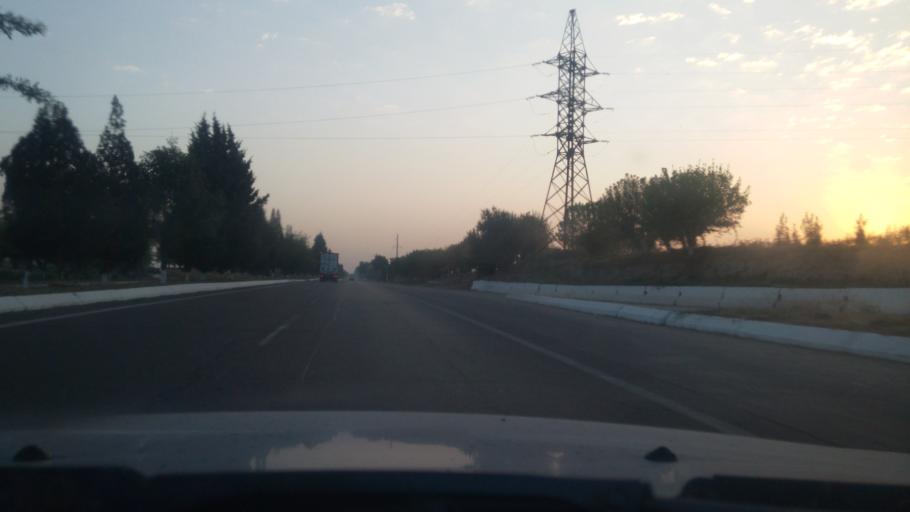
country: UZ
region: Toshkent
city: Zafar
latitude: 41.0258
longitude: 68.8603
